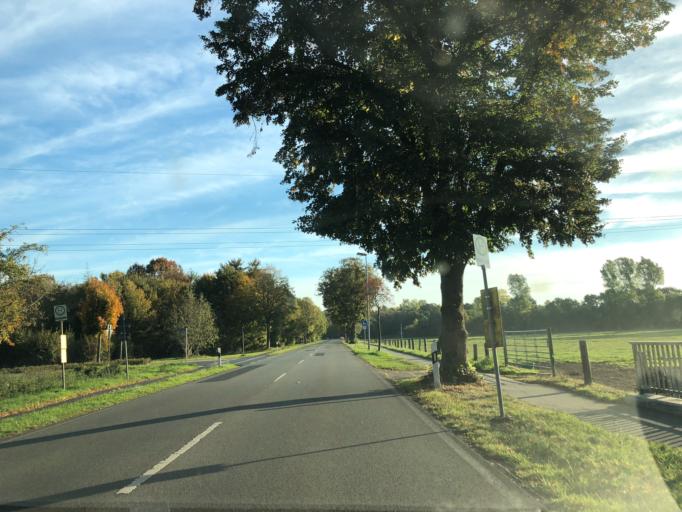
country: DE
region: Lower Saxony
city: Papenburg
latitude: 53.0664
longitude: 7.3683
